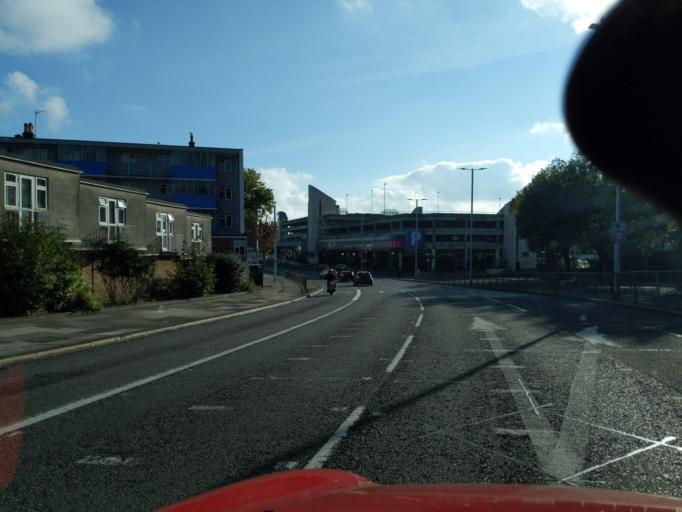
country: GB
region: England
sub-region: Plymouth
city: Plymouth
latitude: 50.3725
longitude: -4.1482
